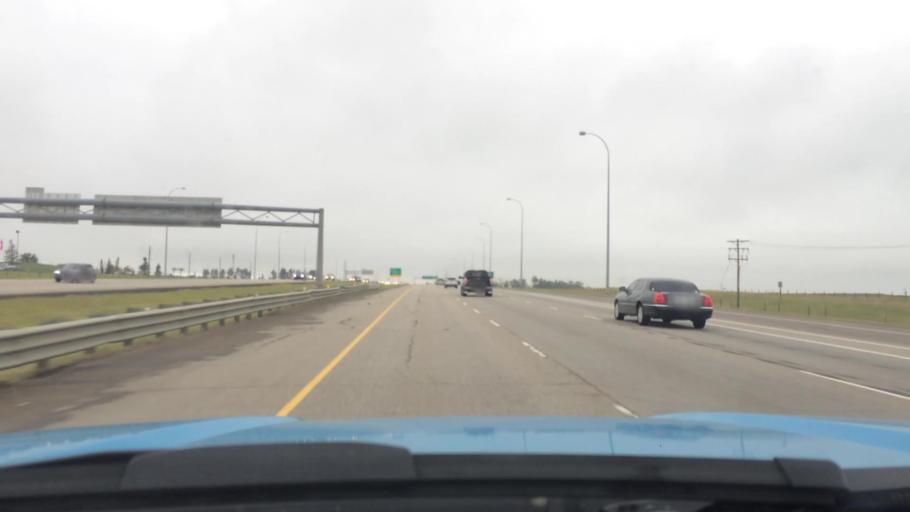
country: CA
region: Alberta
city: Airdrie
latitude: 51.1938
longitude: -114.0017
